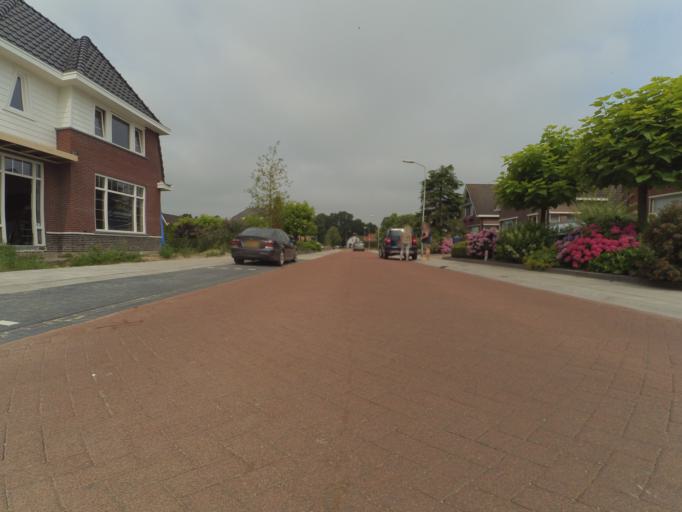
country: NL
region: Gelderland
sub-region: Gemeente Barneveld
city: Kootwijkerbroek
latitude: 52.1502
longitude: 5.6642
